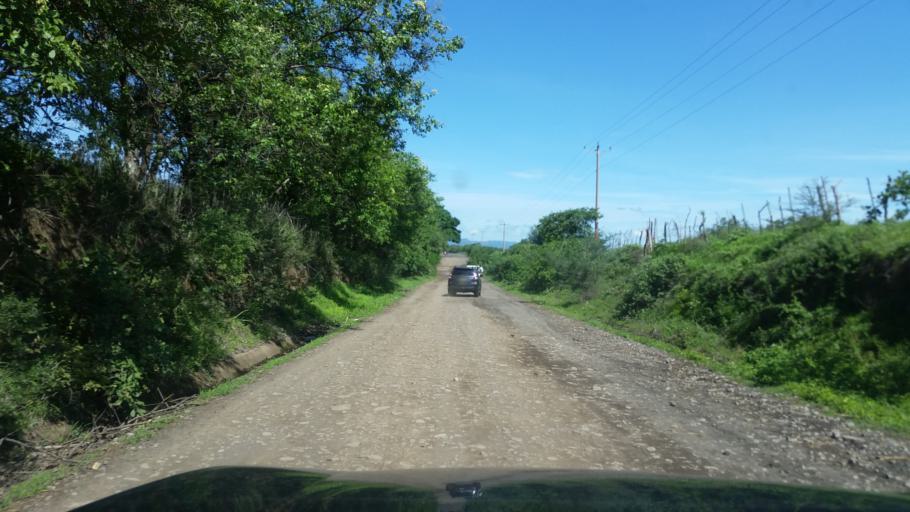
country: NI
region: Chinandega
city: Puerto Morazan
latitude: 12.7674
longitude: -87.0610
